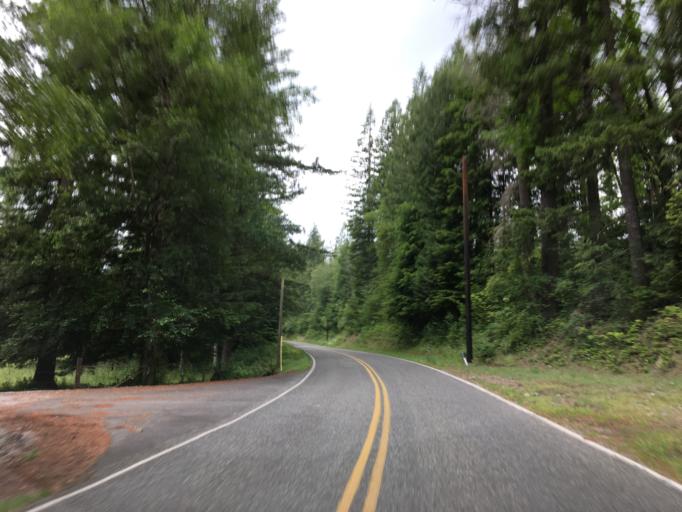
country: US
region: Washington
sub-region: Whatcom County
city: Peaceful Valley
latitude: 48.9776
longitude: -122.1364
